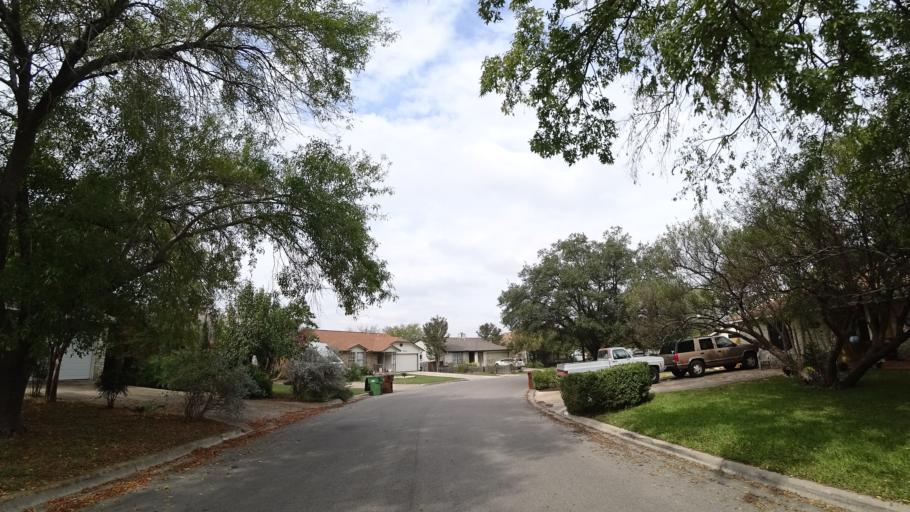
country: US
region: Texas
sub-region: Williamson County
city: Round Rock
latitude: 30.4894
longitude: -97.6886
